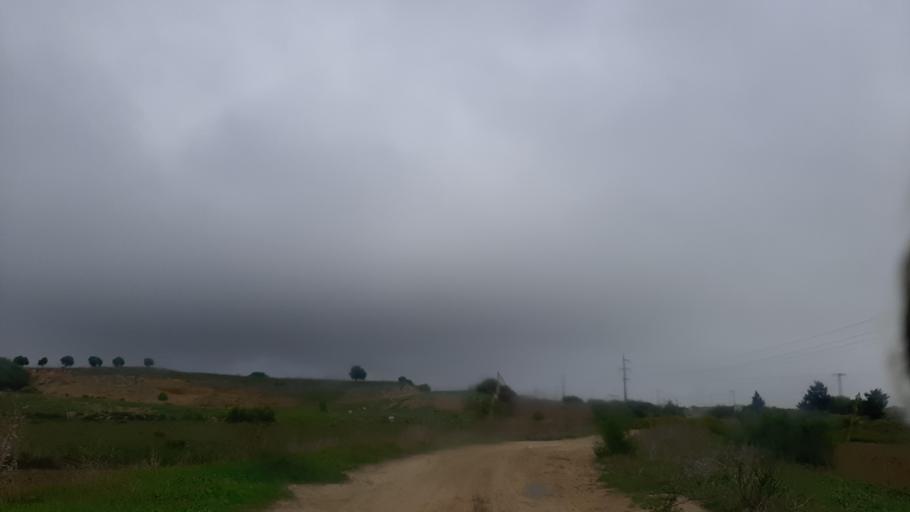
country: TN
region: Nabul
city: Qulaybiyah
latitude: 36.8237
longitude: 11.0479
